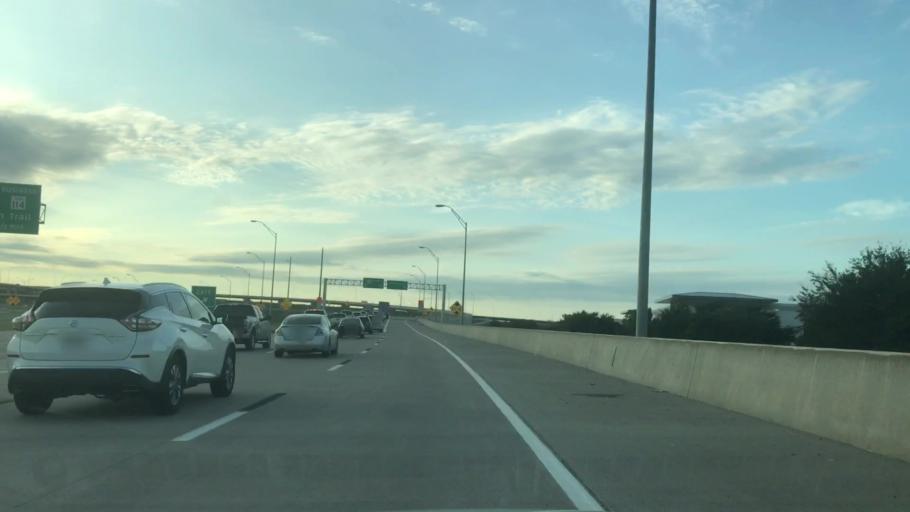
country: US
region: Texas
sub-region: Dallas County
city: Coppell
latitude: 32.9310
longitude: -97.0329
